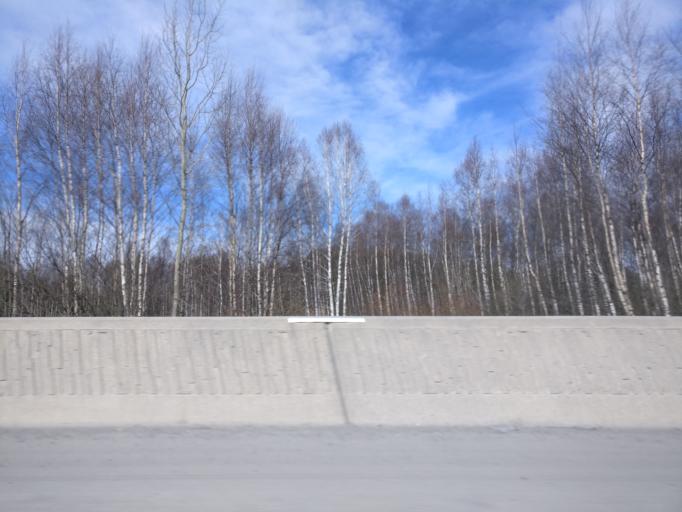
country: FI
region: Haeme
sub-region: Haemeenlinna
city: Parola
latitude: 61.0803
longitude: 24.2539
